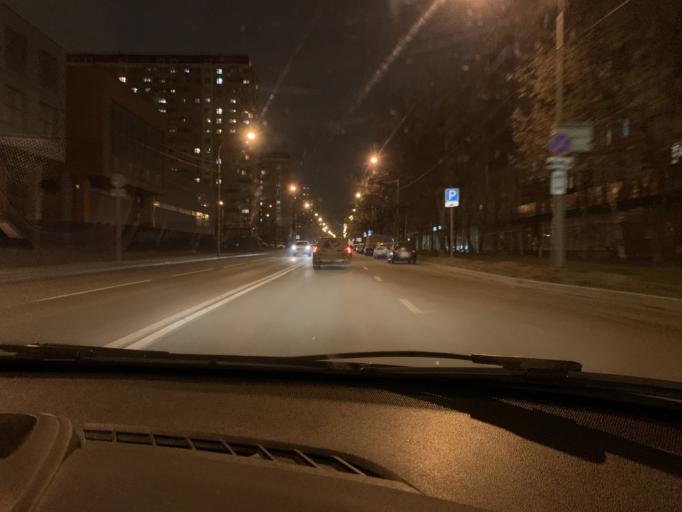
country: RU
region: Moskovskaya
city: Vostochnoe Degunino
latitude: 55.8684
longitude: 37.5630
